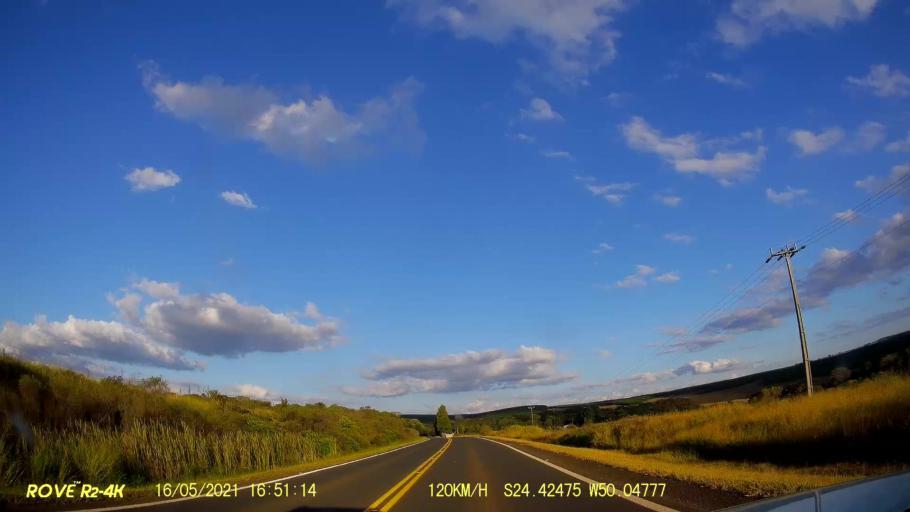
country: BR
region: Parana
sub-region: Pirai Do Sul
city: Pirai do Sul
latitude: -24.4249
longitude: -50.0475
